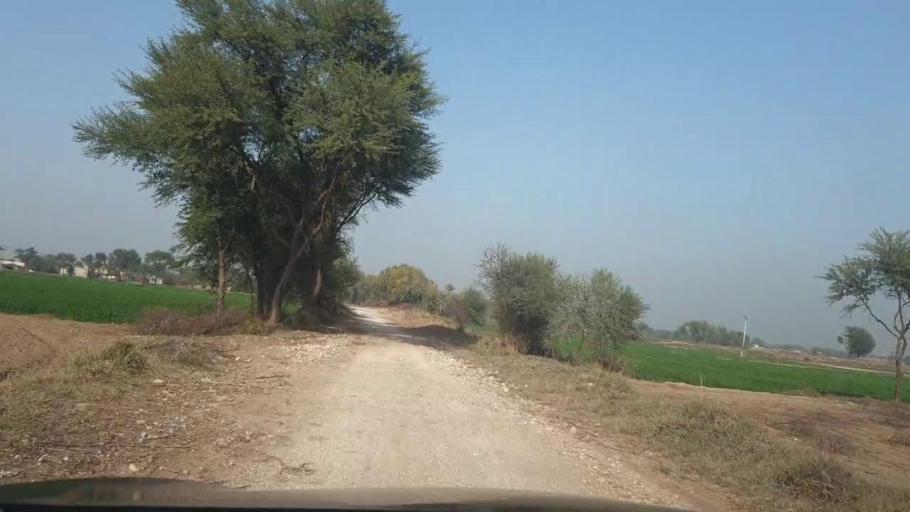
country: PK
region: Sindh
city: Ubauro
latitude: 28.0924
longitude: 69.8412
